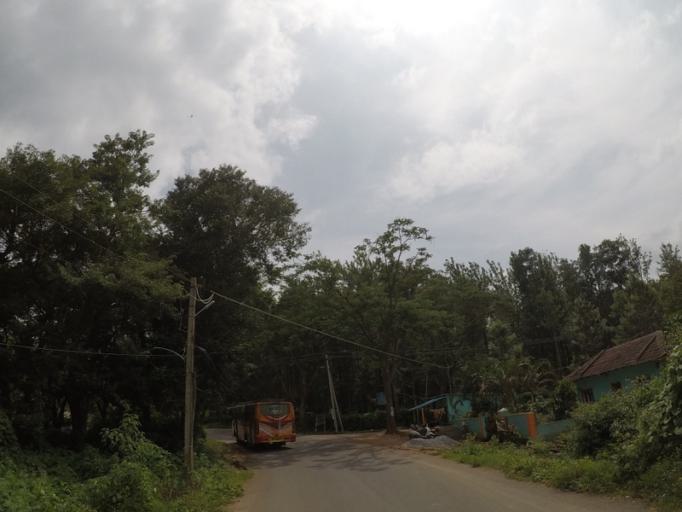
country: IN
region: Karnataka
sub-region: Chikmagalur
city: Chikmagalur
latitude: 13.4395
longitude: 75.8048
